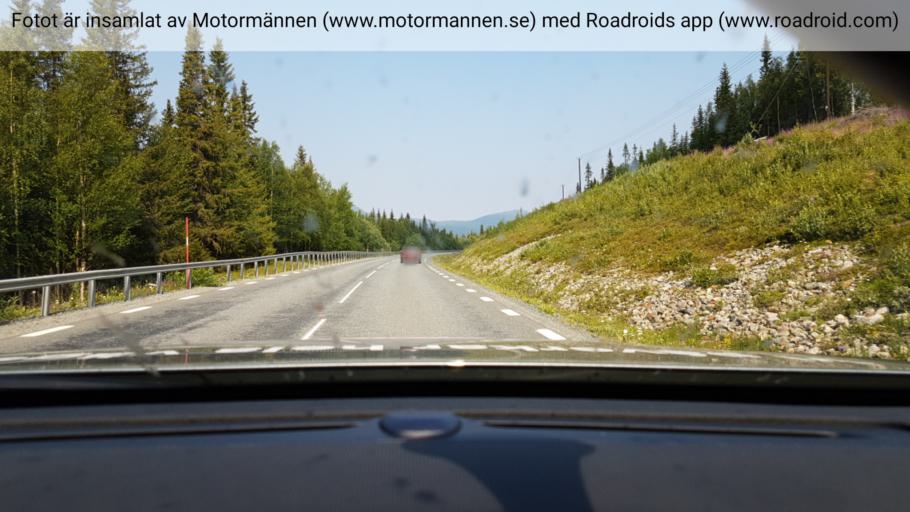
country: SE
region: Vaesterbotten
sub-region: Vilhelmina Kommun
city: Sjoberg
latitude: 65.5565
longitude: 15.5432
